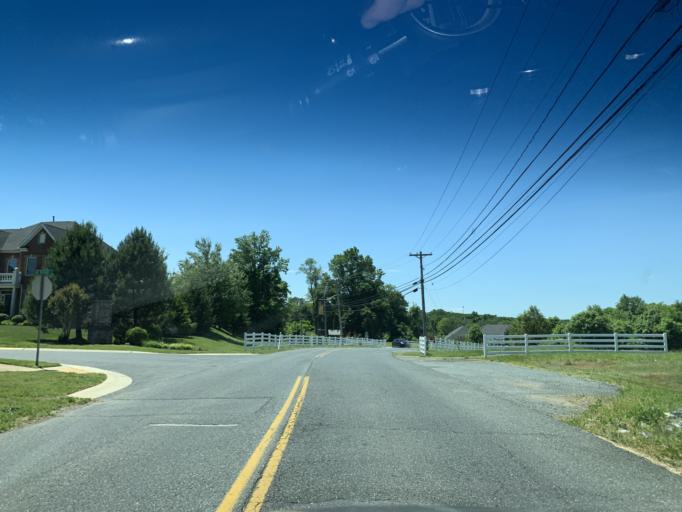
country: US
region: Maryland
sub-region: Harford County
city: Havre de Grace
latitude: 39.5555
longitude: -76.1297
